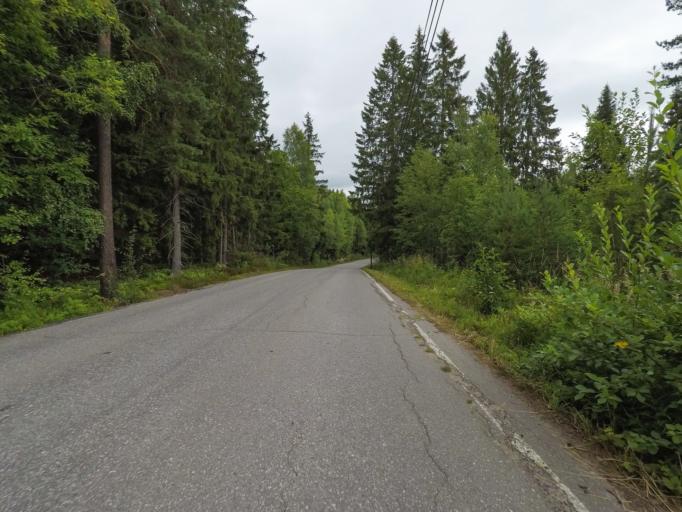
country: FI
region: Uusimaa
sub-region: Helsinki
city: Karjalohja
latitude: 60.2622
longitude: 23.6908
